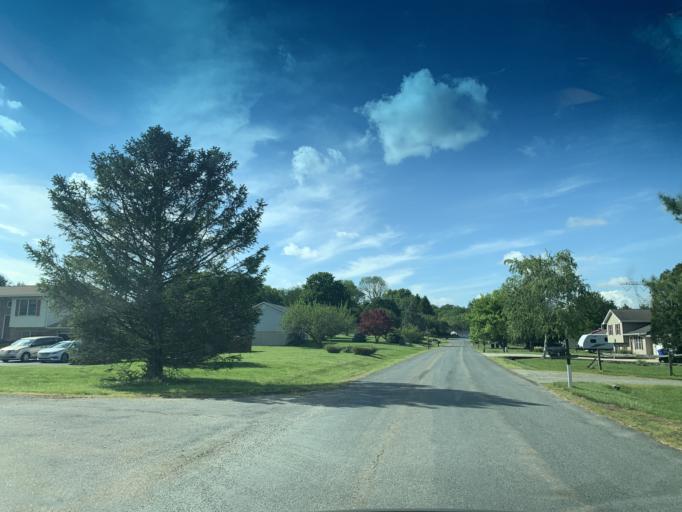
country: US
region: Maryland
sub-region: Cecil County
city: Rising Sun
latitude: 39.6947
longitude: -76.1444
